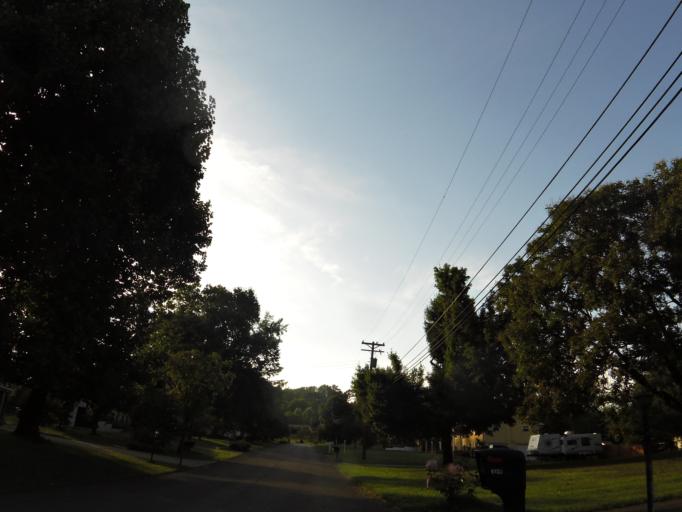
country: US
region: Tennessee
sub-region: Knox County
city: Knoxville
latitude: 35.8817
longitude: -83.9325
